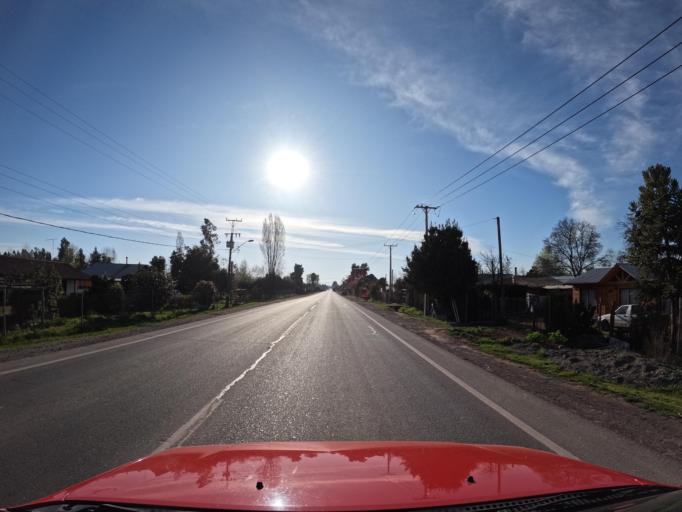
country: CL
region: Maule
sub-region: Provincia de Curico
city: Teno
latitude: -34.9492
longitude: -70.9893
